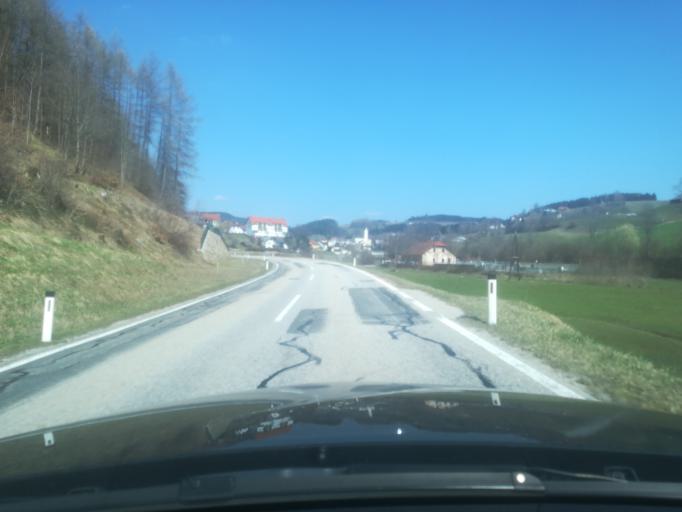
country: AT
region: Upper Austria
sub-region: Politischer Bezirk Perg
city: Sankt Georgen am Walde
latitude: 48.4276
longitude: 14.7759
